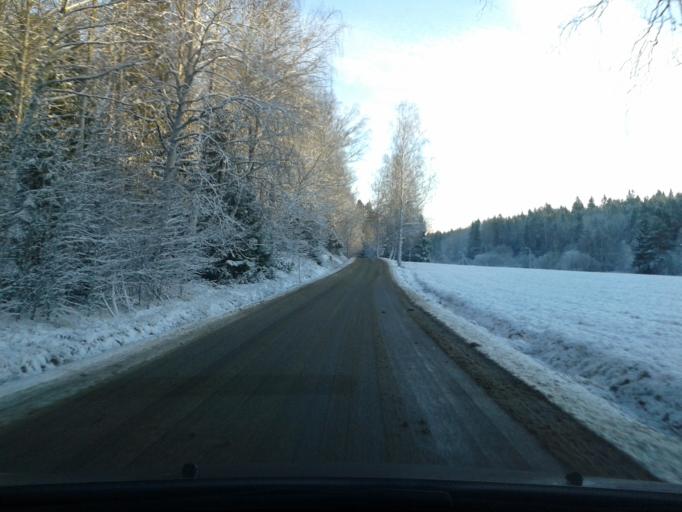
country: SE
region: Stockholm
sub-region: Haninge Kommun
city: Haninge
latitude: 59.1680
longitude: 18.2150
